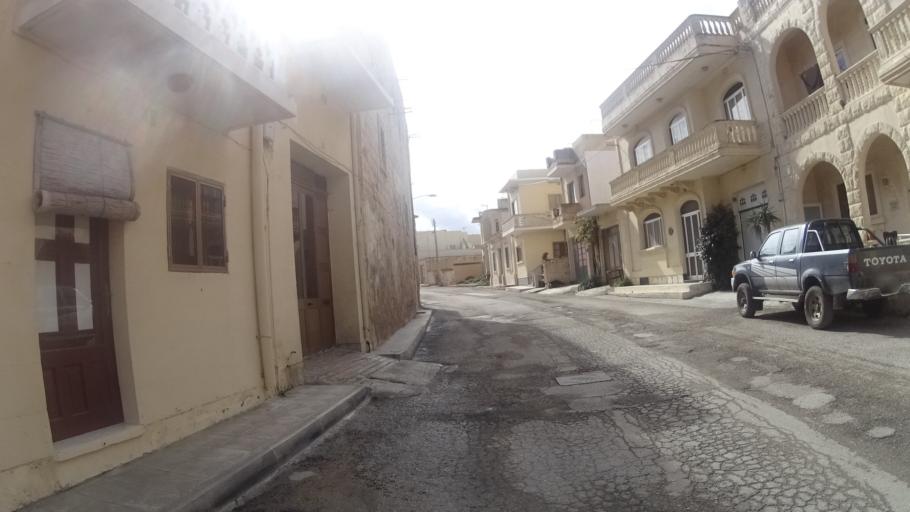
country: MT
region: In-Nadur
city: Nadur
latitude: 36.0443
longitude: 14.2986
